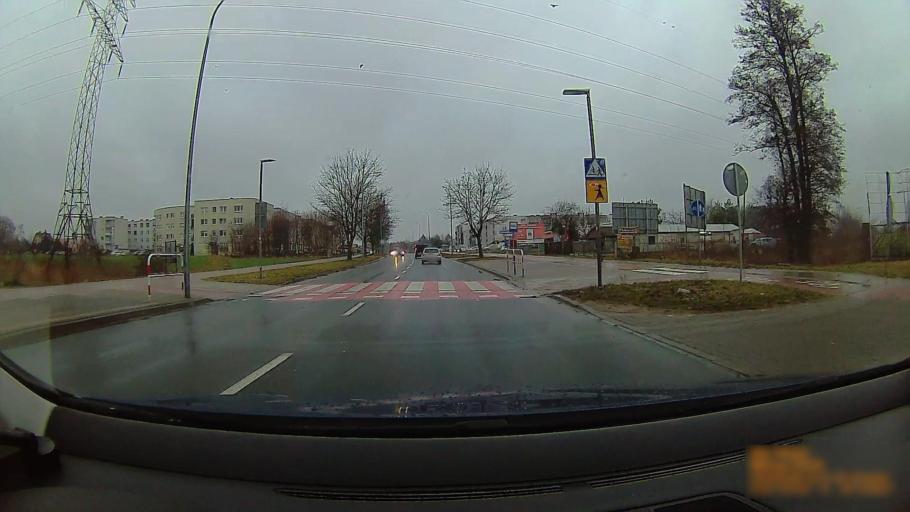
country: PL
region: Greater Poland Voivodeship
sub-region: Konin
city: Konin
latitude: 52.2333
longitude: 18.2249
